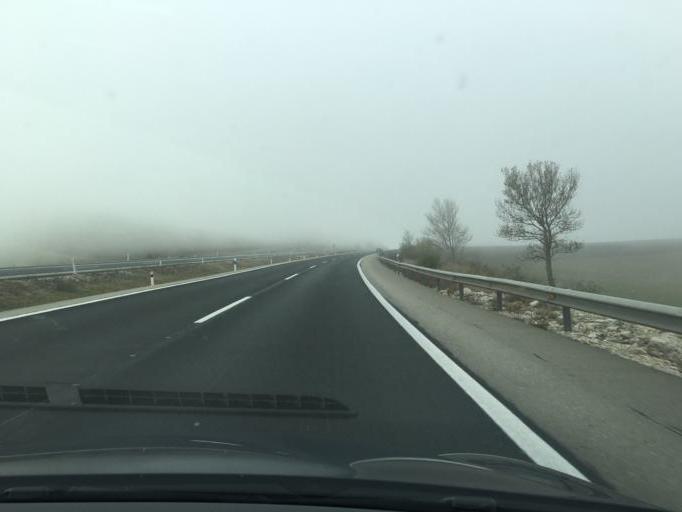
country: ES
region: Castille and Leon
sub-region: Provincia de Burgos
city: Villanueva de Teba
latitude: 42.6237
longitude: -3.1435
